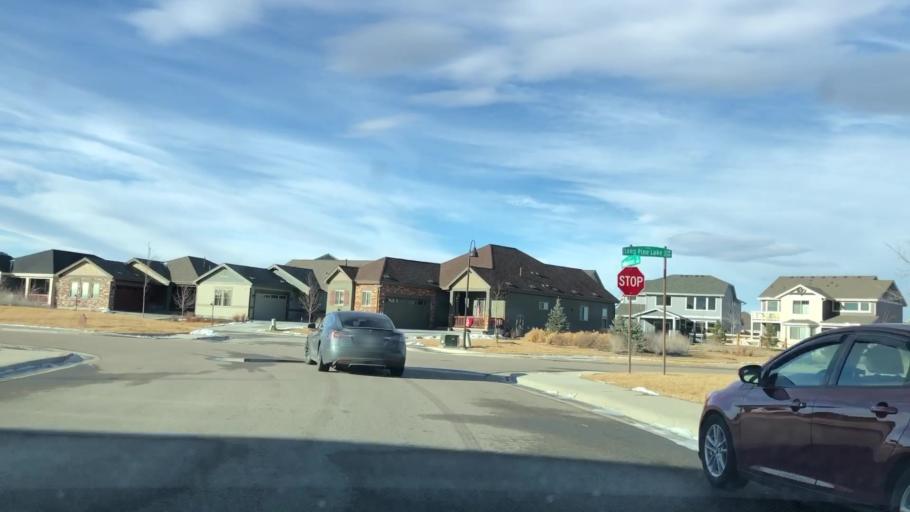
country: US
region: Colorado
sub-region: Larimer County
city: Loveland
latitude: 40.4180
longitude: -105.0171
